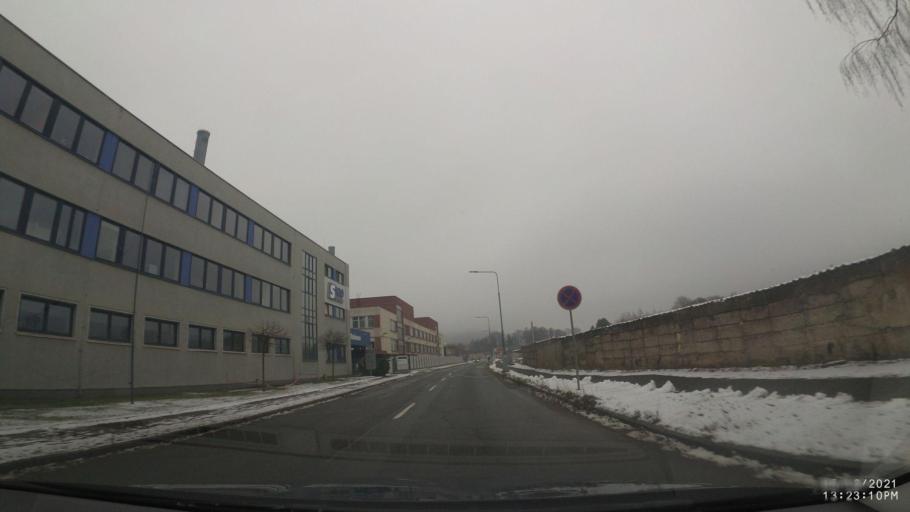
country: CZ
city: Hronov
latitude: 50.4697
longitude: 16.1803
